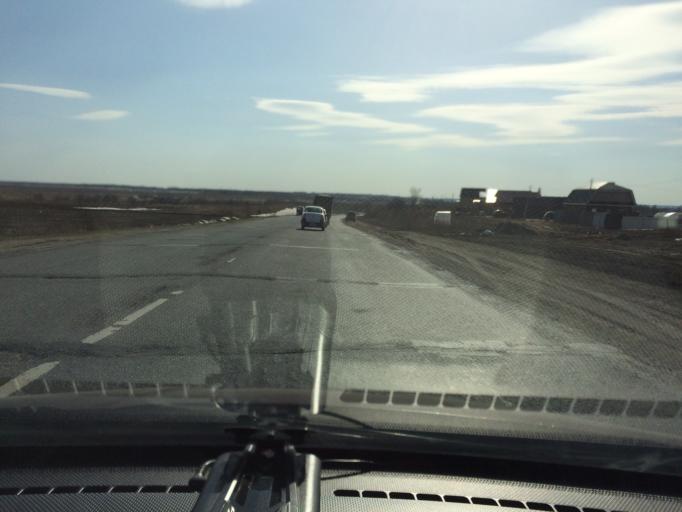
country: RU
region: Mariy-El
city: Yoshkar-Ola
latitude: 56.6928
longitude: 48.0542
